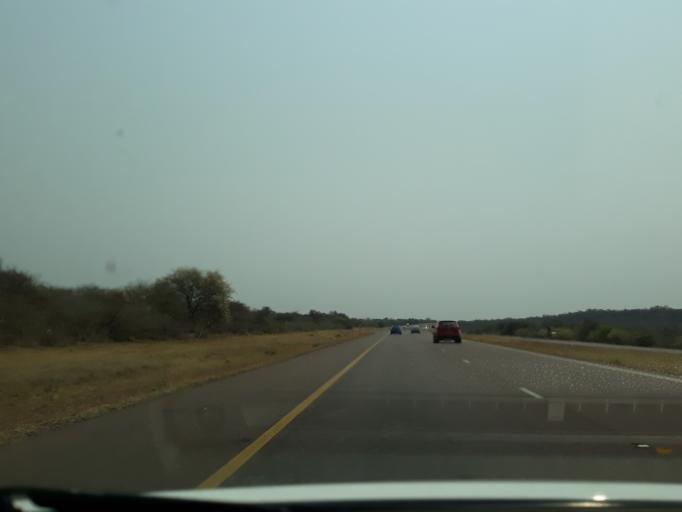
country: BW
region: Kgatleng
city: Bokaa
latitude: -24.4280
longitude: 26.0471
